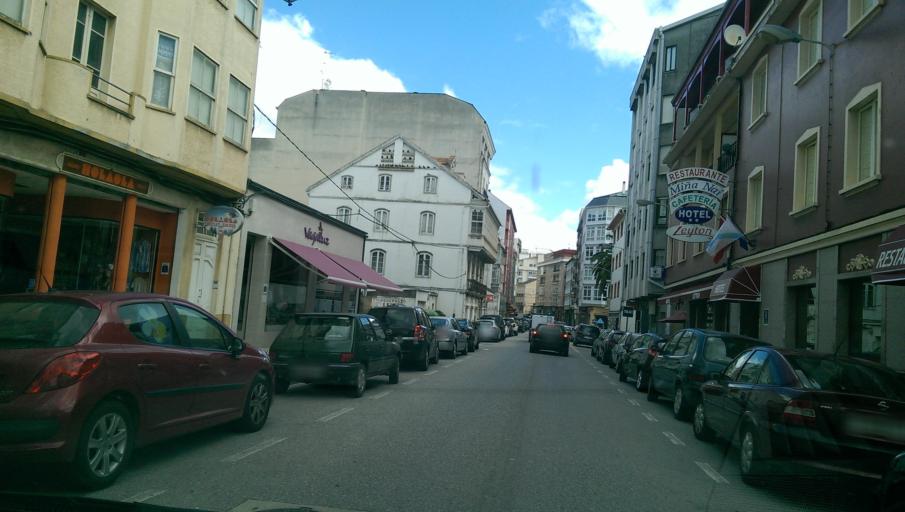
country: ES
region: Galicia
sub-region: Provincia de Lugo
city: Foz
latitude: 43.5664
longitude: -7.2600
